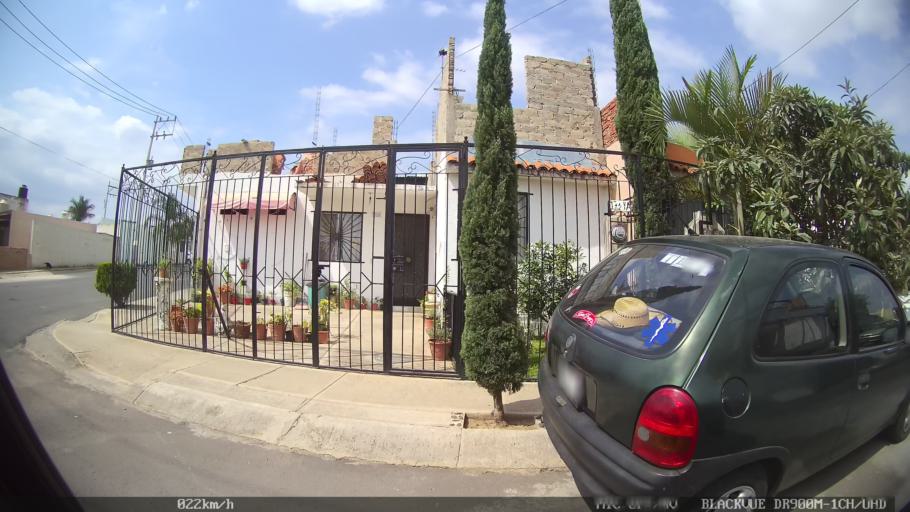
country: MX
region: Jalisco
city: Coyula
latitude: 20.6406
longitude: -103.2169
